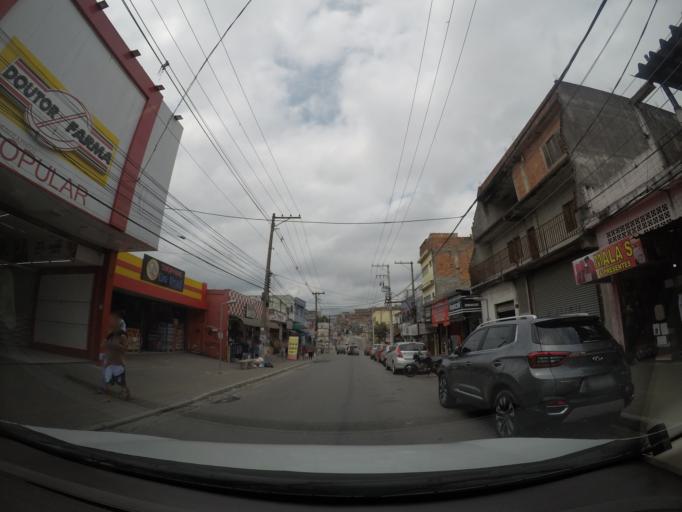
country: BR
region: Sao Paulo
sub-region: Itaquaquecetuba
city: Itaquaquecetuba
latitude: -23.4385
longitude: -46.3839
